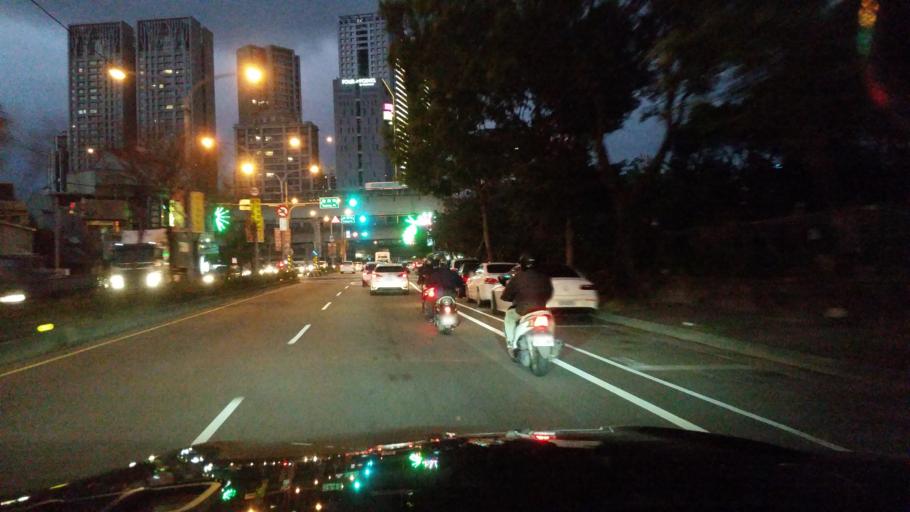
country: TW
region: Taiwan
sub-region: Taoyuan
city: Taoyuan
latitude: 25.0630
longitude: 121.3613
